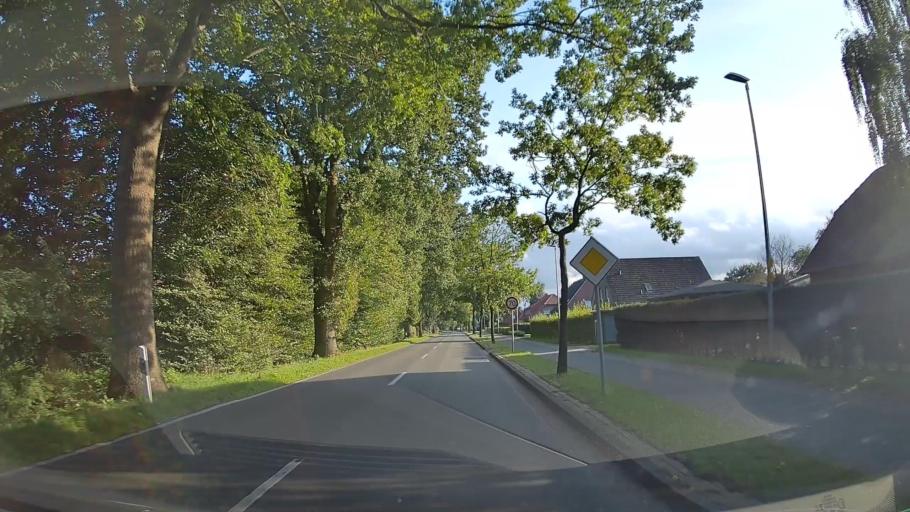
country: DE
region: Lower Saxony
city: Hilkenbrook
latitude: 53.0329
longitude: 7.7459
